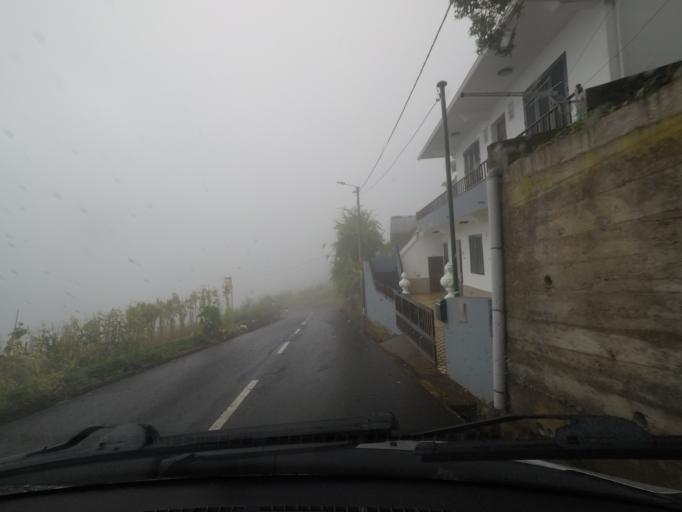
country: PT
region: Madeira
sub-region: Santana
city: Santana
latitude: 32.7728
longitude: -16.8734
